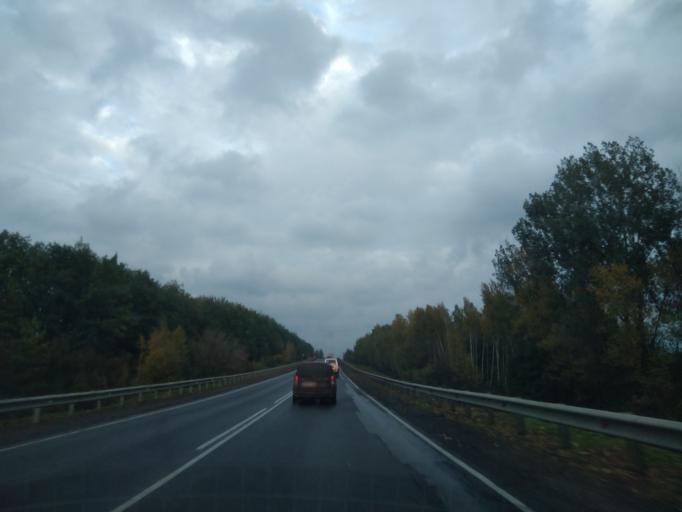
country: RU
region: Lipetsk
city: Borinskoye
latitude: 52.6018
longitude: 39.3383
